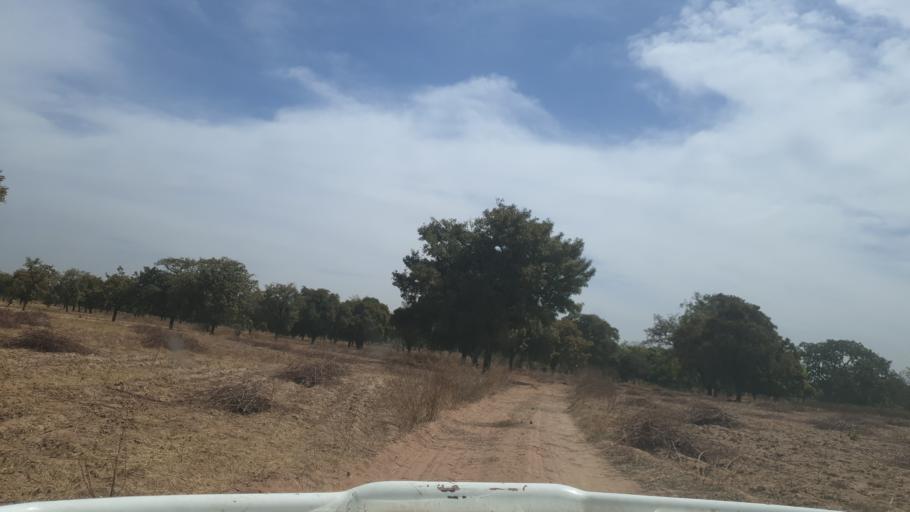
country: ML
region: Sikasso
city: Yorosso
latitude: 12.2876
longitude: -4.6758
